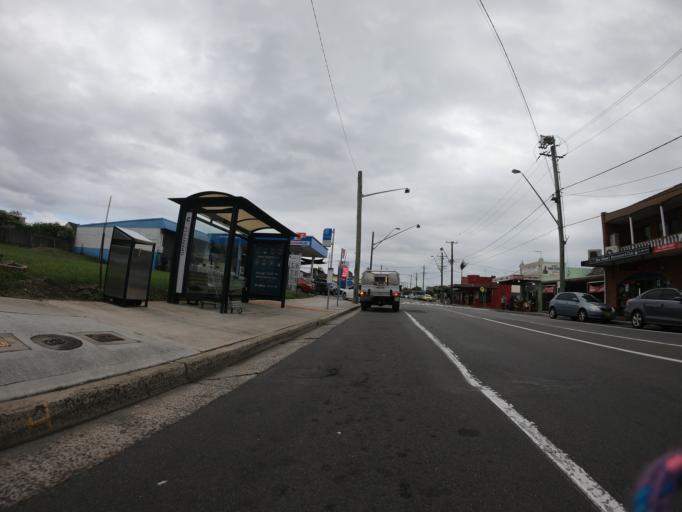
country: AU
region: New South Wales
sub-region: Parramatta
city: Granville
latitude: -33.8423
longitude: 151.0104
